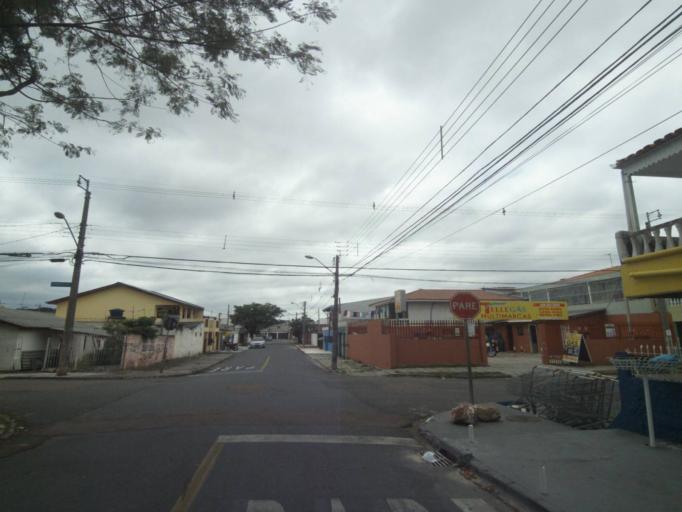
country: BR
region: Parana
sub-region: Sao Jose Dos Pinhais
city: Sao Jose dos Pinhais
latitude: -25.5346
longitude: -49.2605
